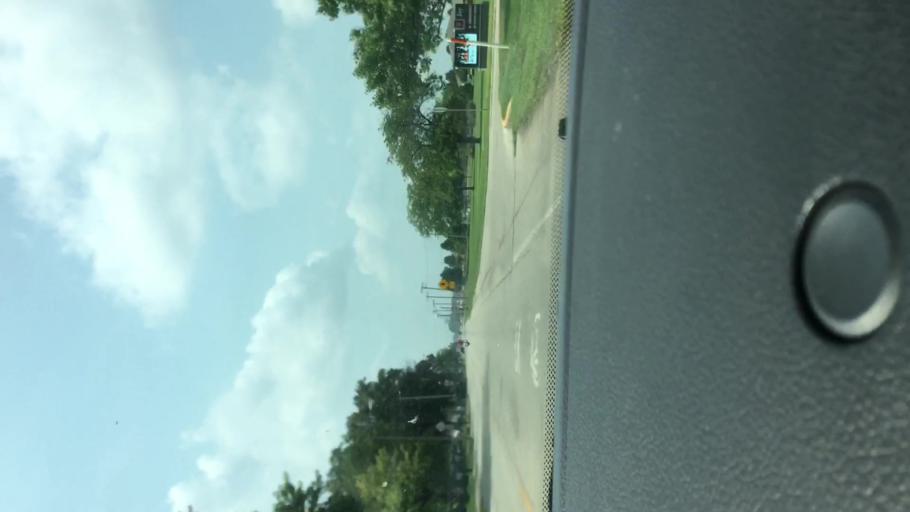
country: US
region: Indiana
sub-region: Jay County
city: Portland
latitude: 40.4394
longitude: -84.9838
